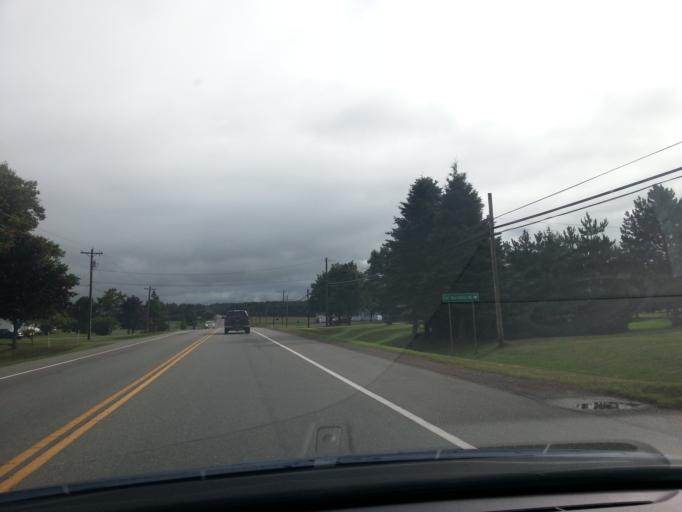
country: CA
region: Prince Edward Island
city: Charlottetown
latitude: 46.2921
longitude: -63.0853
